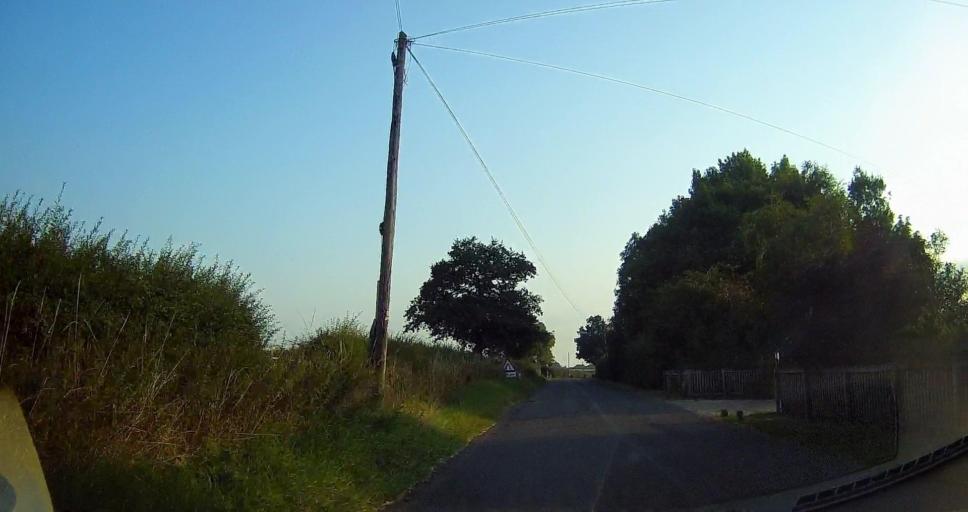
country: GB
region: England
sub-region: Cheshire East
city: Nantwich
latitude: 53.0049
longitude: -2.5294
